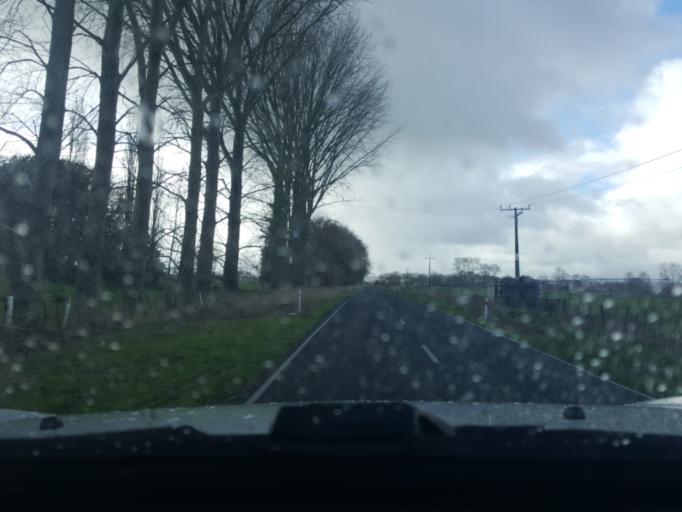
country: NZ
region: Waikato
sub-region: Waikato District
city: Te Kauwhata
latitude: -37.4475
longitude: 175.1083
